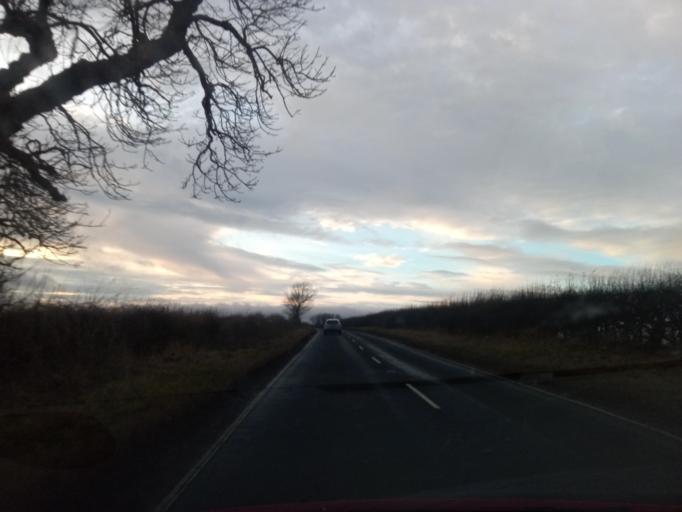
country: GB
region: England
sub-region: Northumberland
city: Ponteland
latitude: 55.0743
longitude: -1.7184
